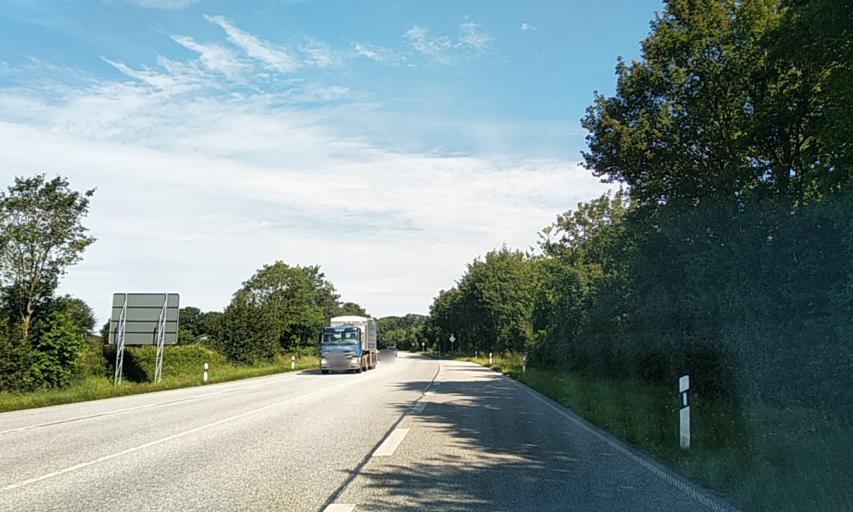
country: DE
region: Schleswig-Holstein
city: Fockbek
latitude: 54.3321
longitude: 9.6207
